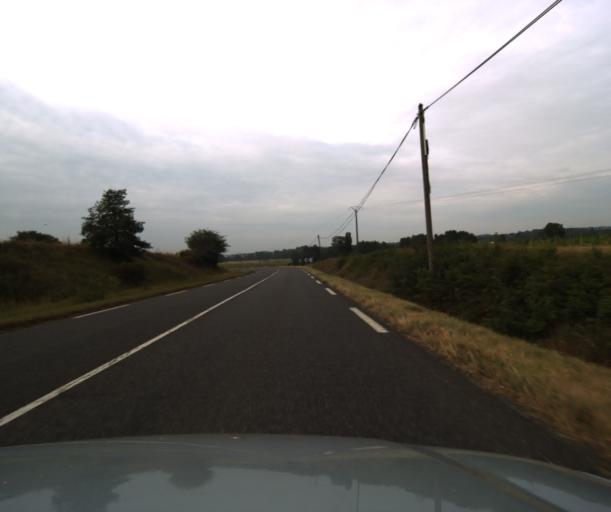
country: FR
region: Midi-Pyrenees
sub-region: Departement du Gers
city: Mirande
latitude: 43.5299
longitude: 0.4168
